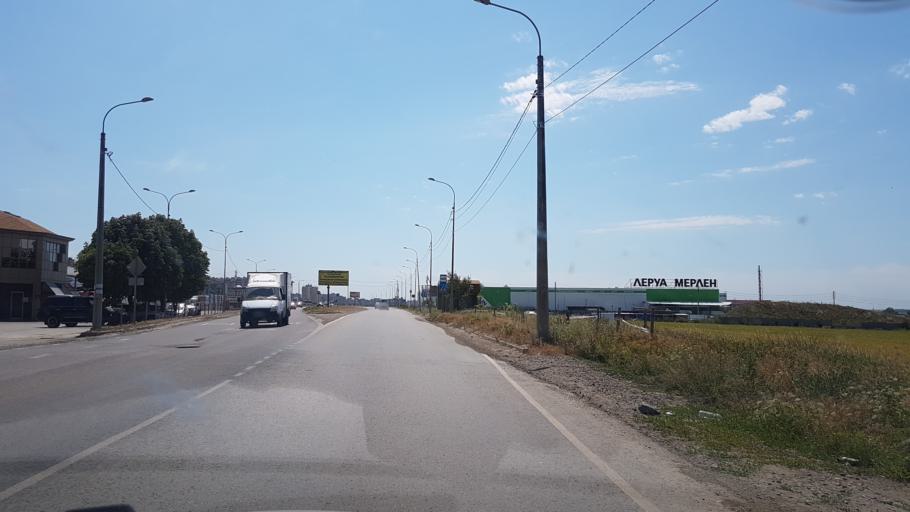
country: RU
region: Rostov
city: Temernik
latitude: 47.3115
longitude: 39.7308
